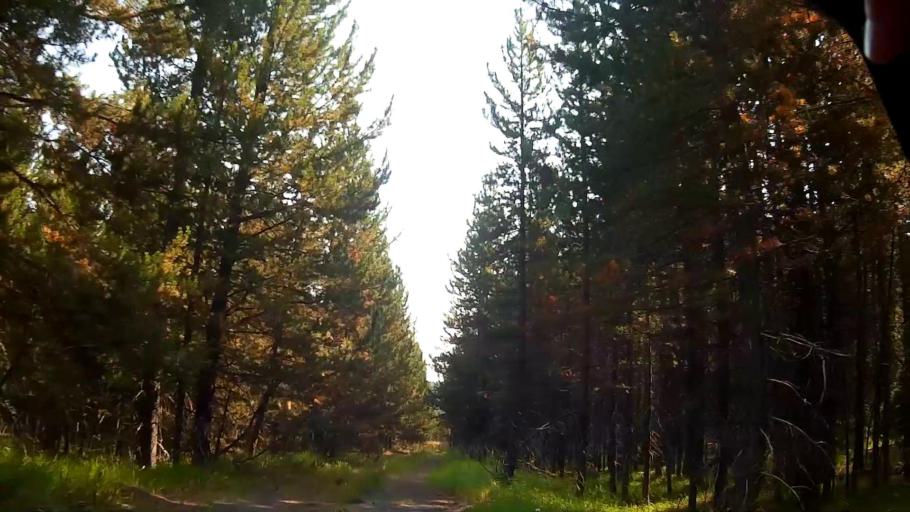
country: US
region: Montana
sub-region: Gallatin County
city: West Yellowstone
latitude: 44.5762
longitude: -111.1815
